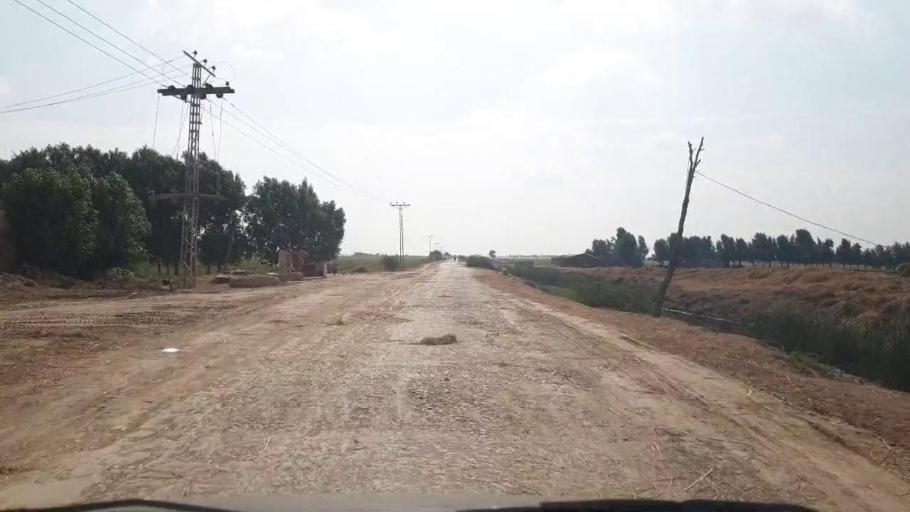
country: PK
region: Sindh
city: Kario
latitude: 24.6365
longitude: 68.5477
